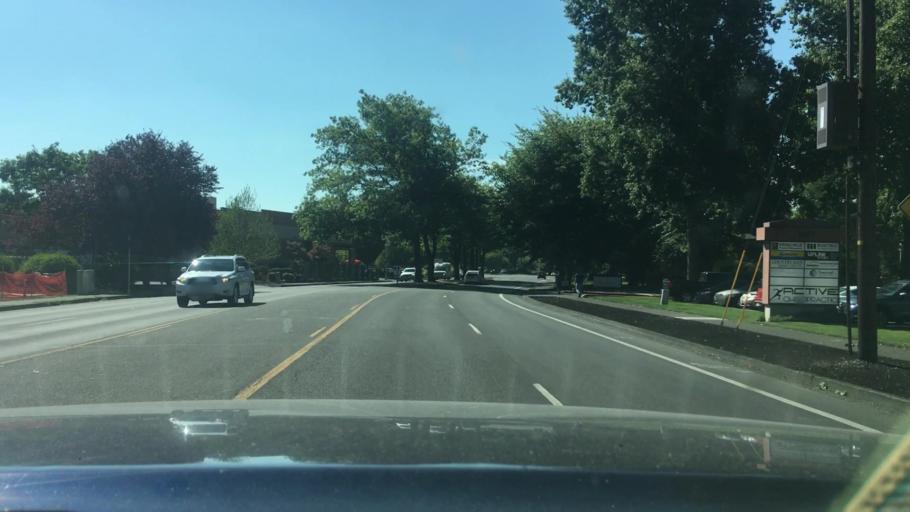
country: US
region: Oregon
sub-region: Lane County
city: Eugene
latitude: 44.0803
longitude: -123.0685
